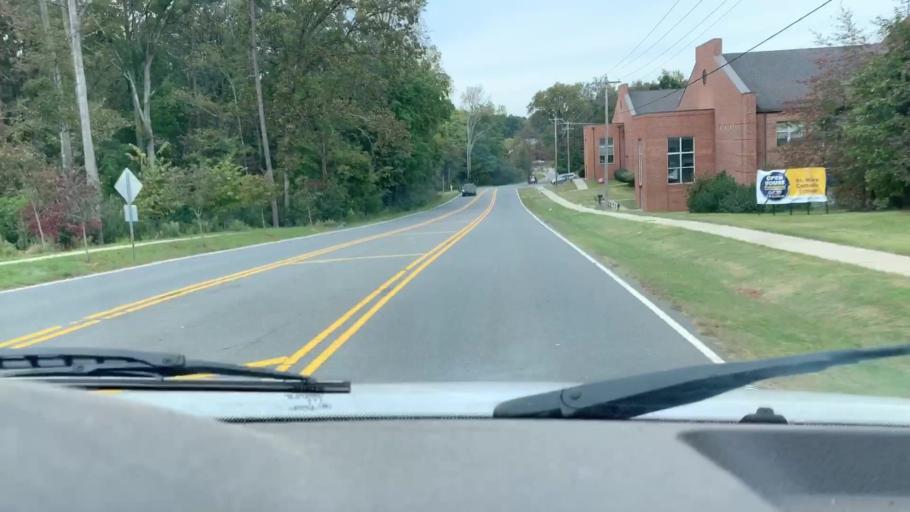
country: US
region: North Carolina
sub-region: Mecklenburg County
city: Huntersville
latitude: 35.4210
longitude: -80.8674
